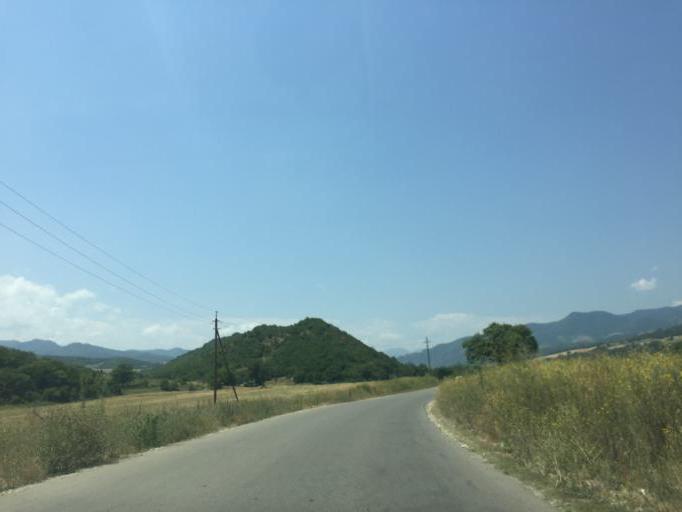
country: AZ
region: Tartar Rayon
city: Martakert
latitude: 40.1377
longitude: 46.5059
